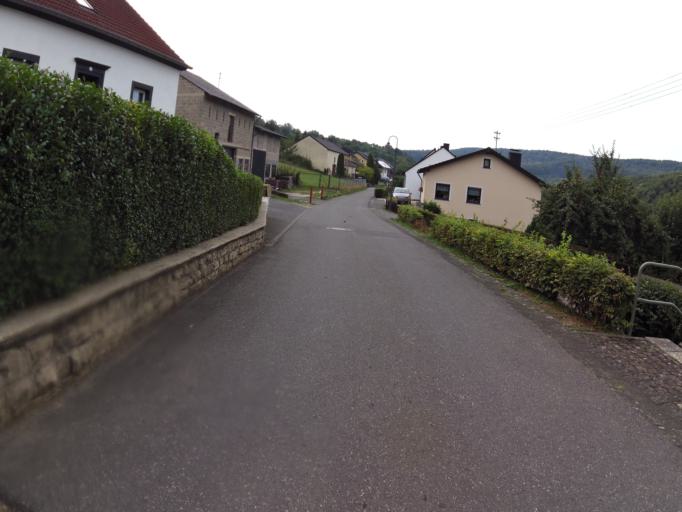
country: DE
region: Rheinland-Pfalz
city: Metterich
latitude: 49.9669
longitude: 6.5884
